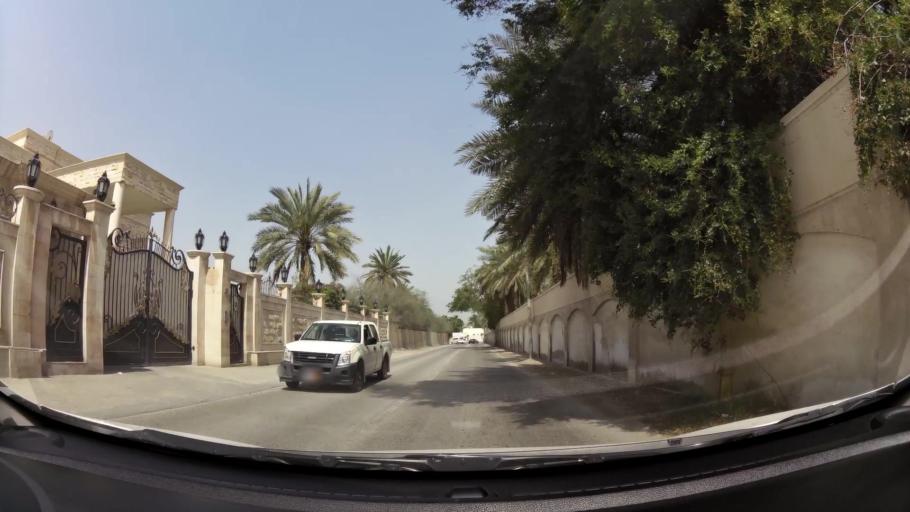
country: BH
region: Manama
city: Jidd Hafs
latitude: 26.2231
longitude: 50.4778
